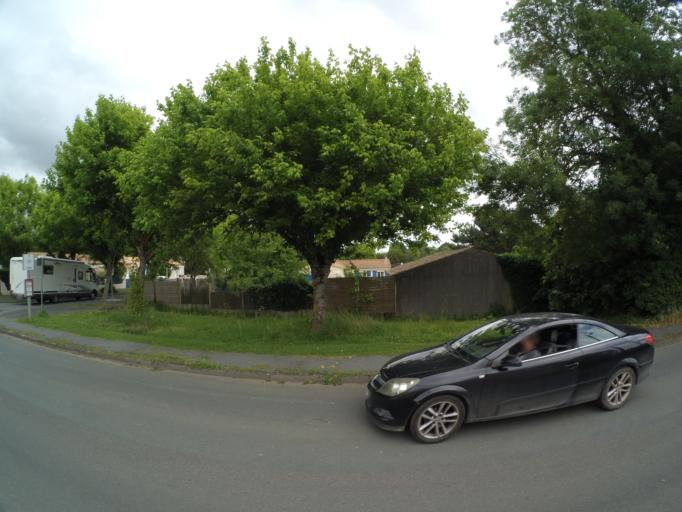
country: FR
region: Poitou-Charentes
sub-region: Departement de la Charente-Maritime
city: Breuil-Magne
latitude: 45.9618
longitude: -0.9698
